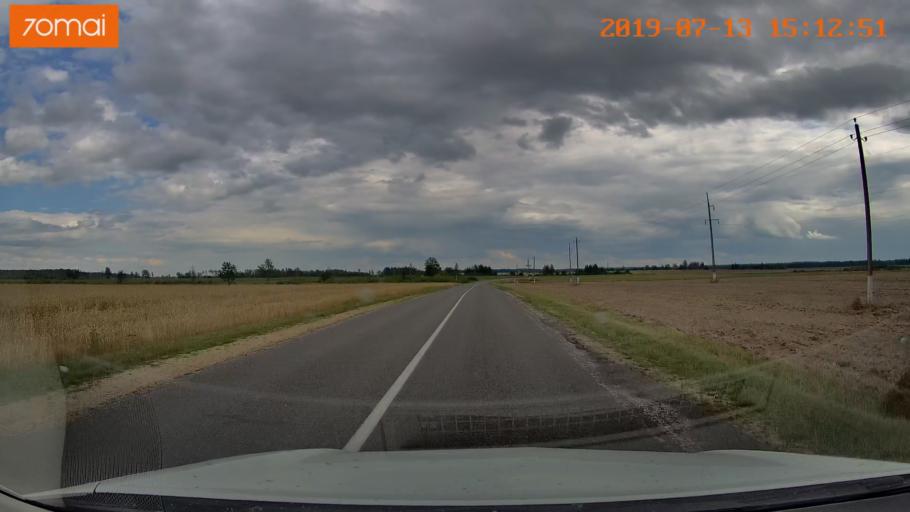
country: BY
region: Mogilev
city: Hlusha
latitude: 53.1443
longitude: 28.7983
